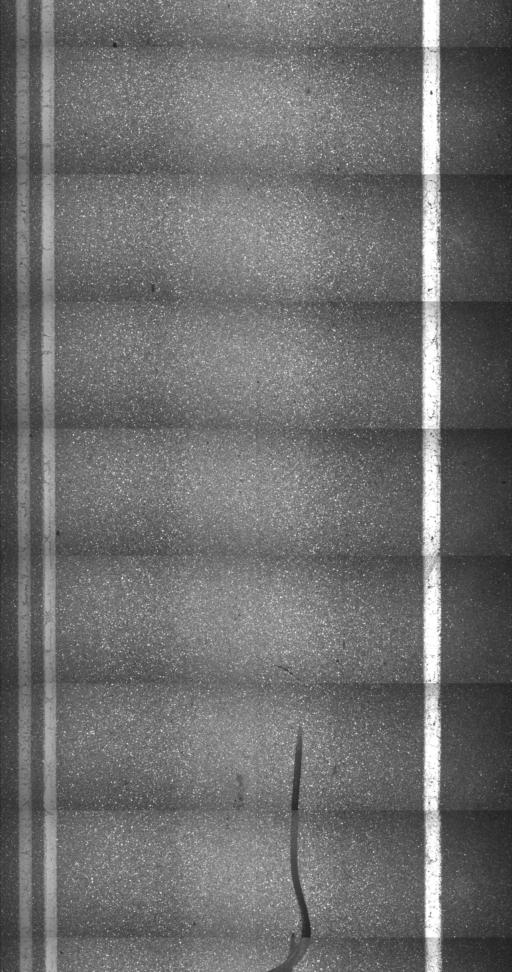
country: US
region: Vermont
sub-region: Rutland County
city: Castleton
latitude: 43.6282
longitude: -73.2040
